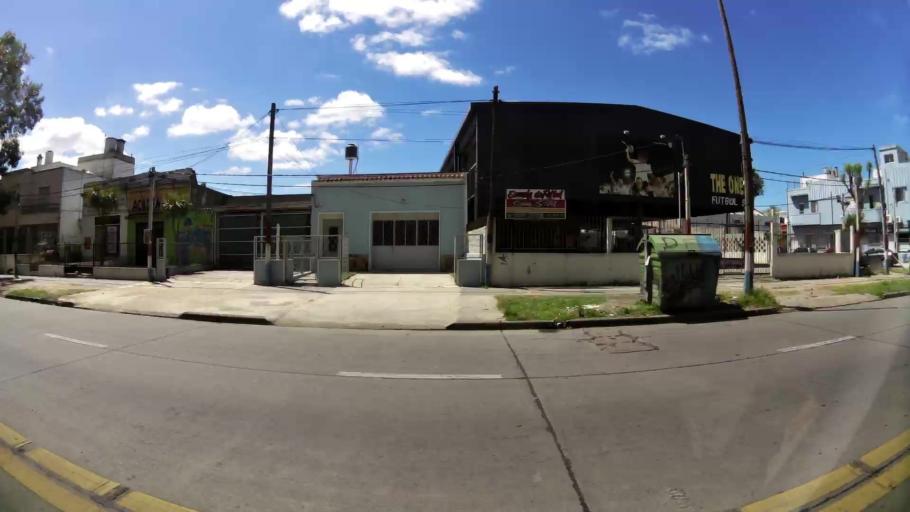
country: UY
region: Montevideo
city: Montevideo
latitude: -34.8542
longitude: -56.1309
